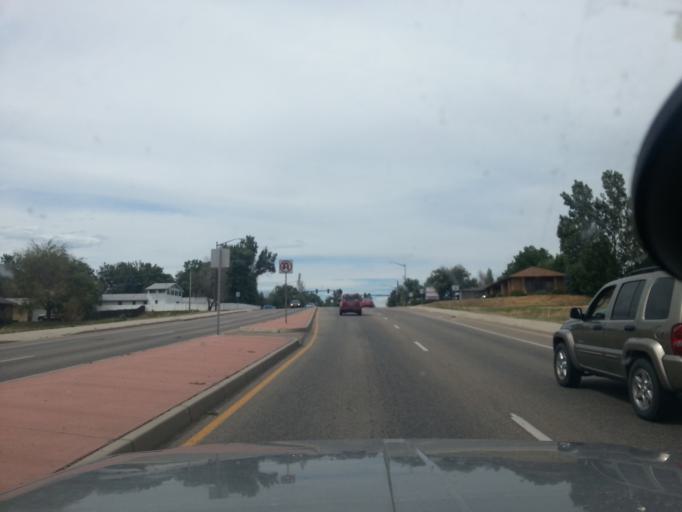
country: US
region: Colorado
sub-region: Larimer County
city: Loveland
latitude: 40.3984
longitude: -105.0969
